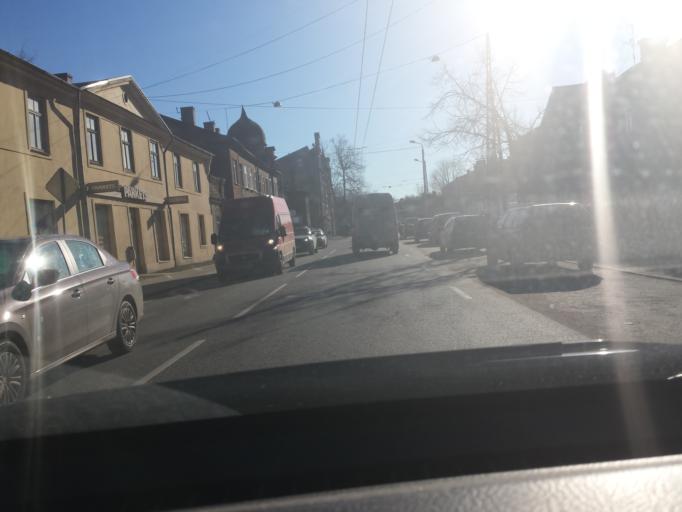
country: LV
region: Riga
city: Riga
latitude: 56.9533
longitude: 24.1515
